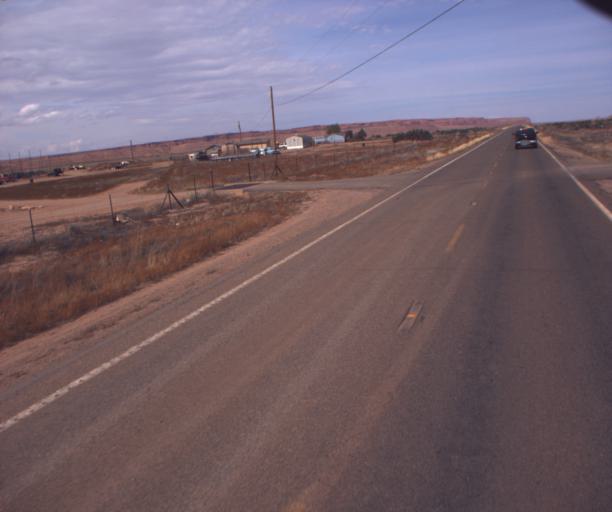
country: US
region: Arizona
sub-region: Apache County
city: Many Farms
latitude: 36.4370
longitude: -109.6071
